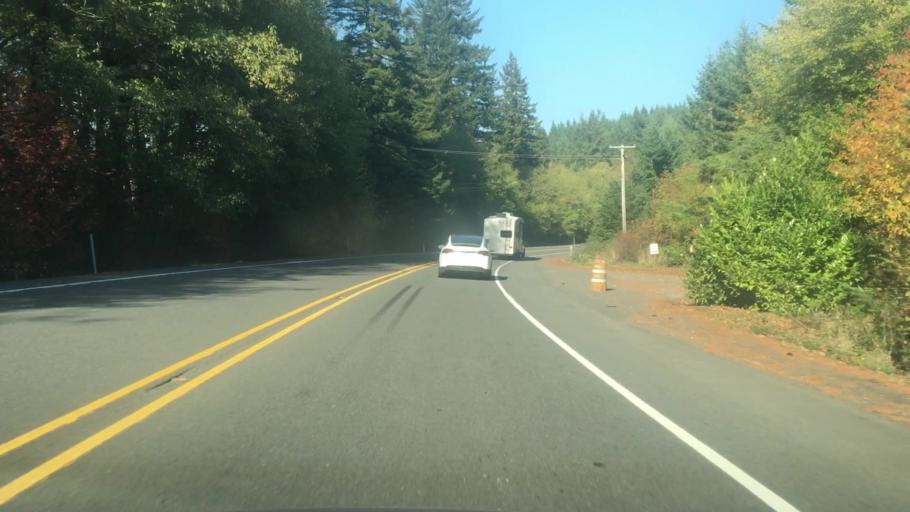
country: US
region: Oregon
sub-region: Polk County
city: Grand Ronde
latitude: 45.0667
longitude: -123.7290
